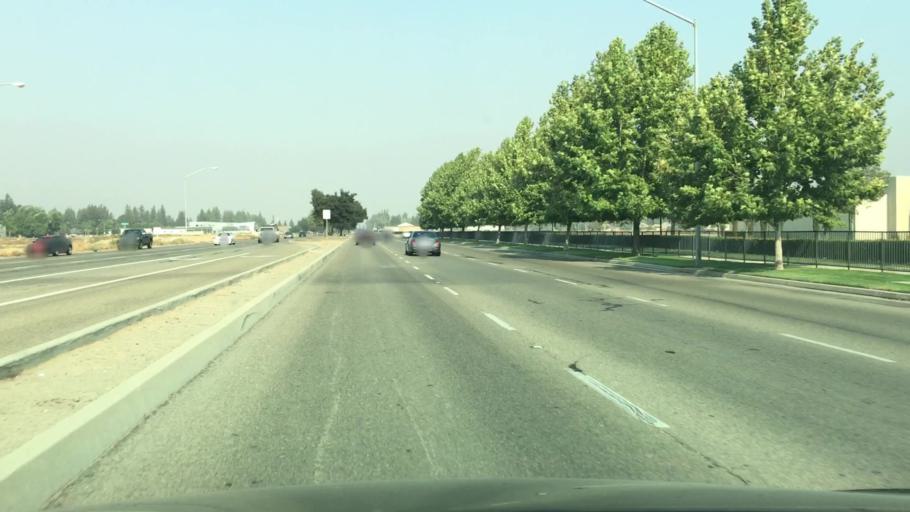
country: US
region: California
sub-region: Fresno County
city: West Park
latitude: 36.8371
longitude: -119.8709
